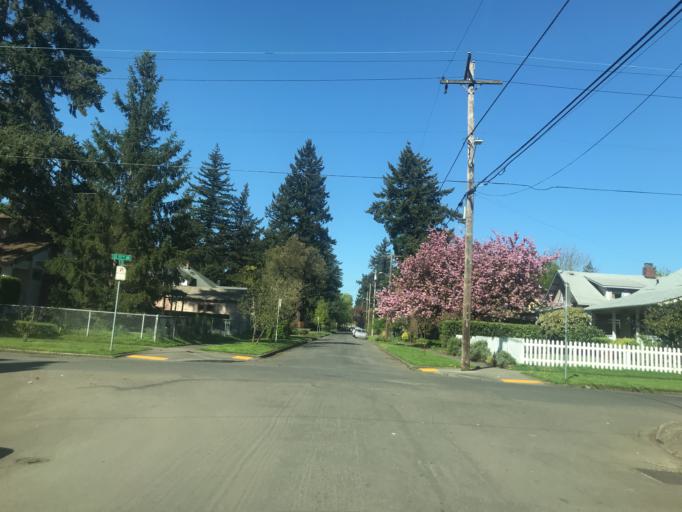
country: US
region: Oregon
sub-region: Multnomah County
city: Lents
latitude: 45.4824
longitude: -122.5839
